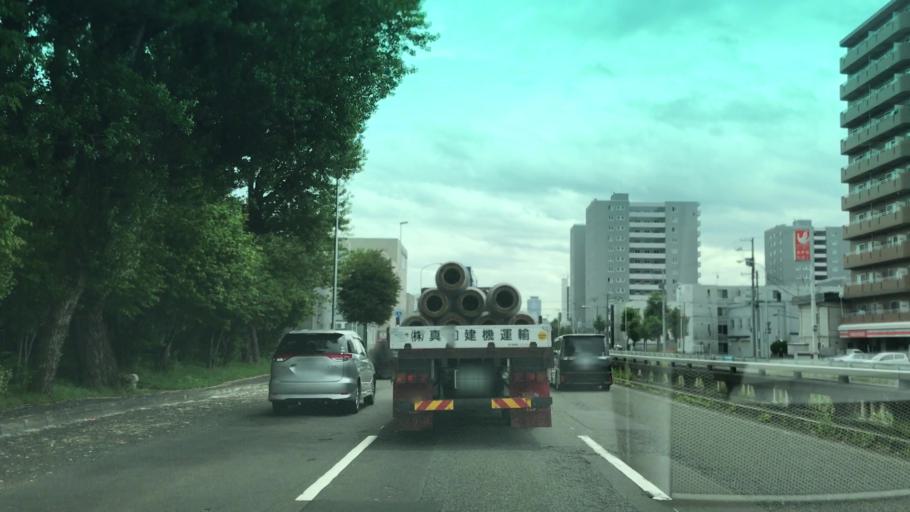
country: JP
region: Hokkaido
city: Sapporo
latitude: 43.0951
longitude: 141.3467
